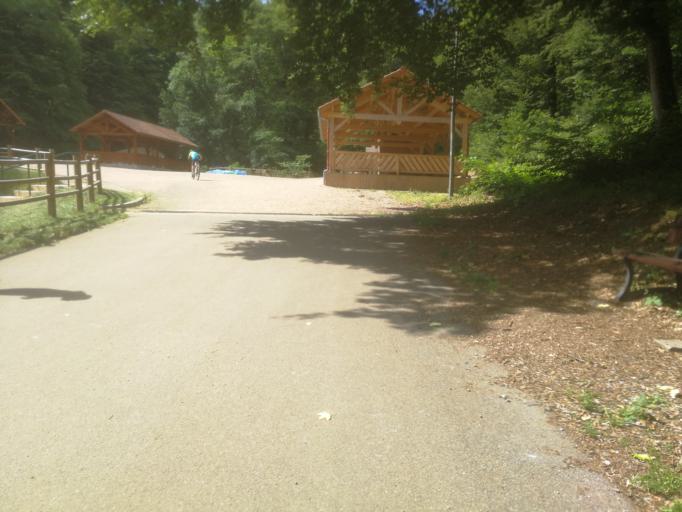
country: FR
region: Lorraine
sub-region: Departement de la Moselle
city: Rosselange
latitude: 49.2364
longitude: 6.0753
